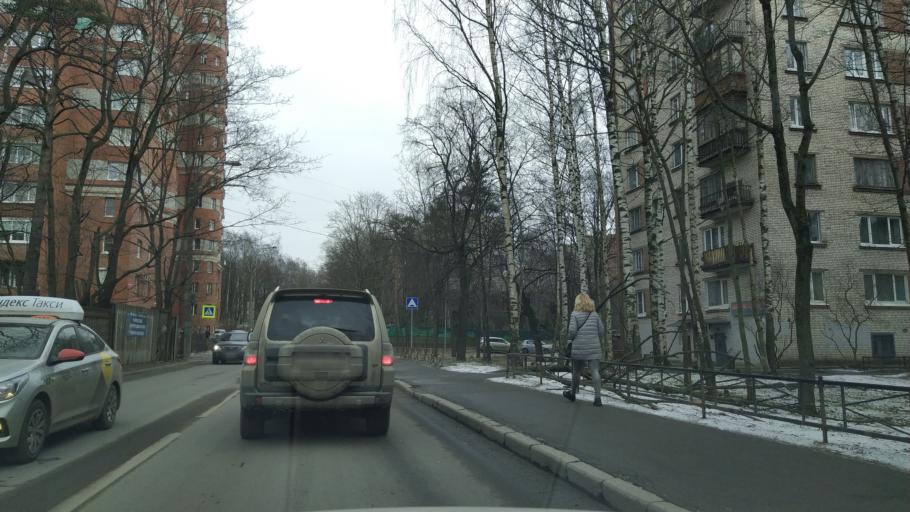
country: RU
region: Leningrad
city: Udel'naya
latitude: 60.0212
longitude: 30.3263
